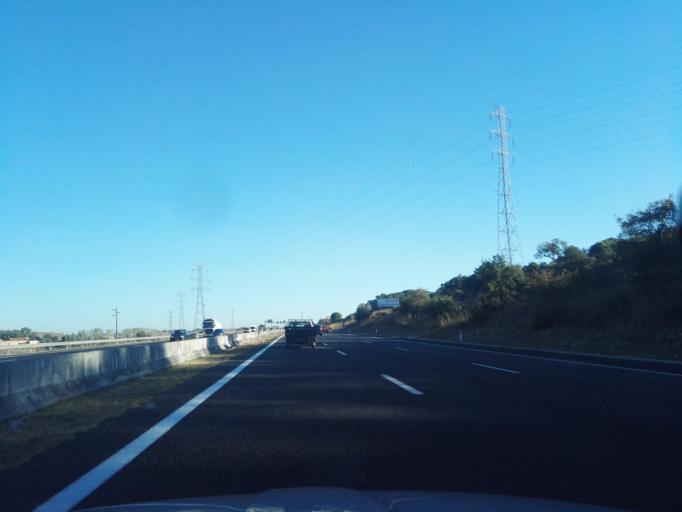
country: PT
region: Santarem
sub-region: Santarem
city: Santarem
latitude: 39.2487
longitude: -8.7402
